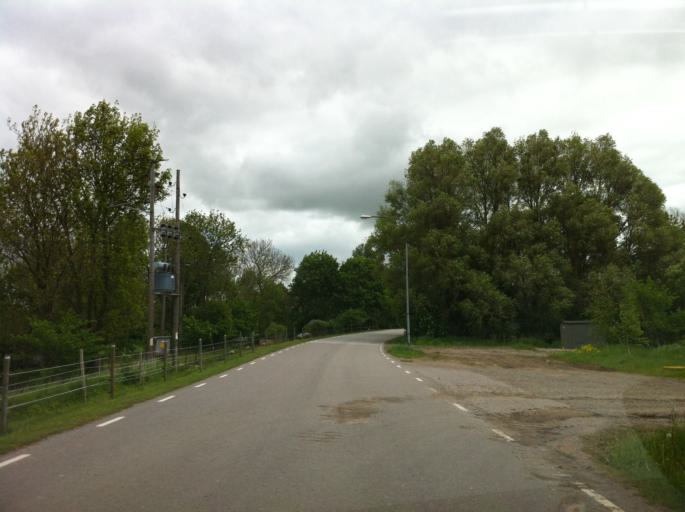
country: SE
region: Skane
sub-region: Kavlinge Kommun
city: Kaevlinge
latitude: 55.8213
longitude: 13.0830
